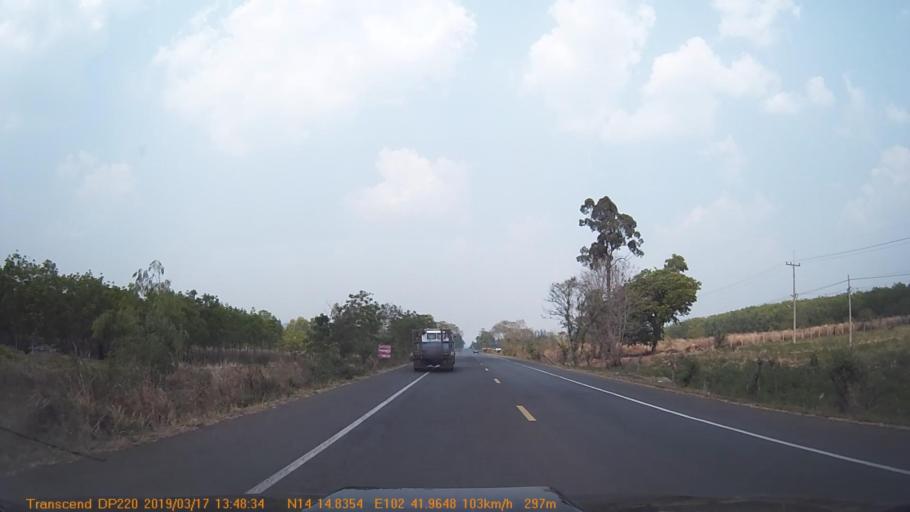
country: TH
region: Buriram
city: Non Din Daeng
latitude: 14.2477
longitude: 102.6997
